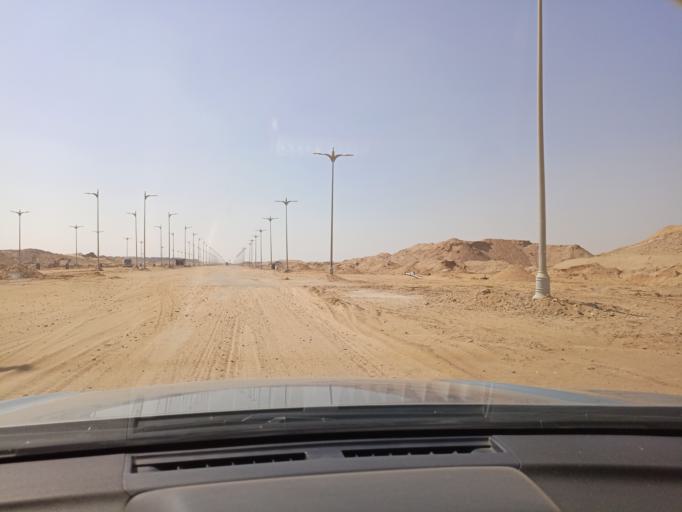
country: EG
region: Muhafazat al Qalyubiyah
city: Al Khankah
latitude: 30.0088
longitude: 31.6190
